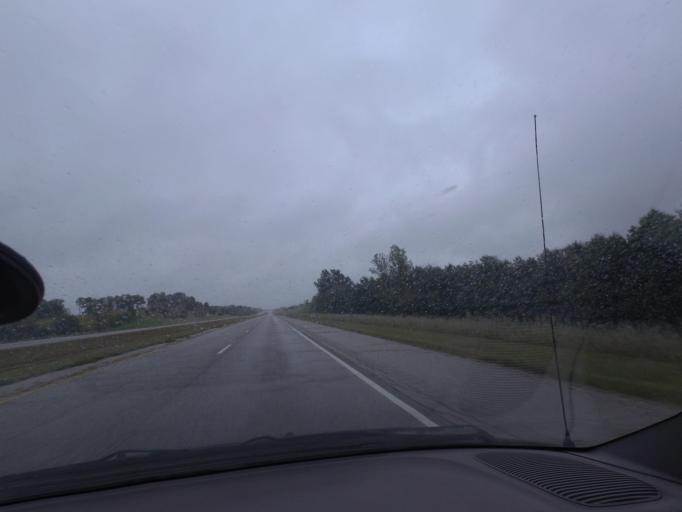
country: US
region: Illinois
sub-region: Pike County
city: Barry
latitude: 39.6909
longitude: -90.9294
